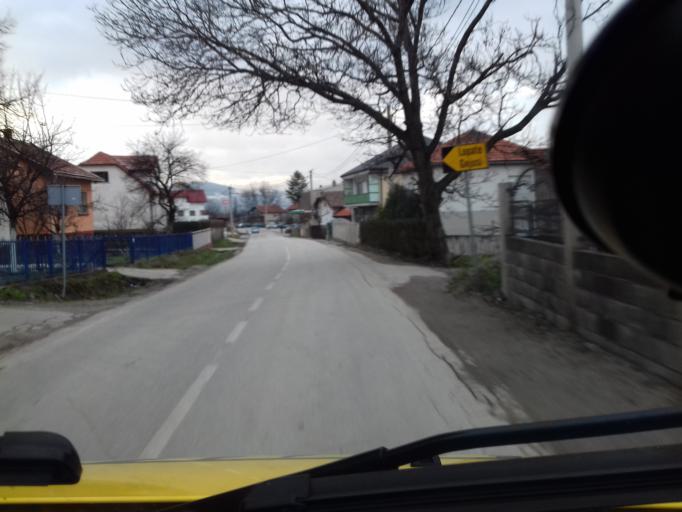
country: BA
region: Federation of Bosnia and Herzegovina
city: Zenica
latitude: 44.1840
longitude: 17.9560
